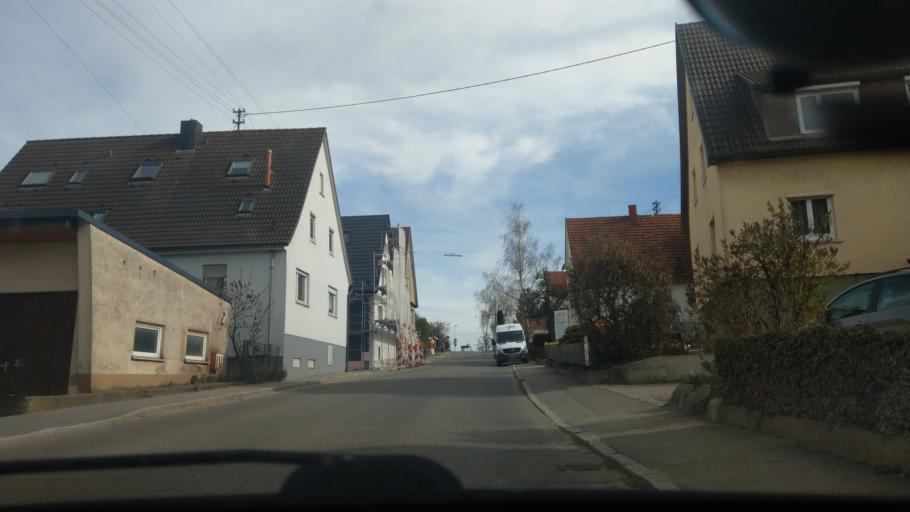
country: DE
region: Baden-Wuerttemberg
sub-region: Regierungsbezirk Stuttgart
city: Filderstadt
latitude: 48.6706
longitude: 9.2422
